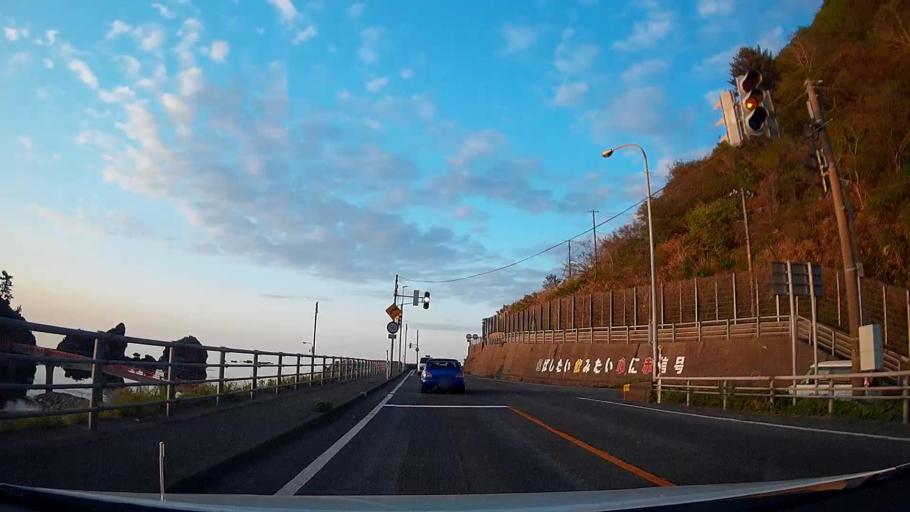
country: JP
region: Niigata
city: Itoigawa
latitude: 37.1078
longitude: 137.9936
